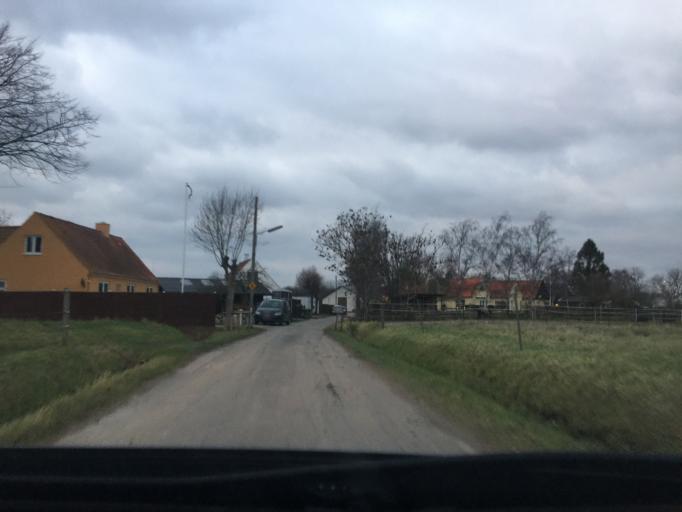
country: DK
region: Capital Region
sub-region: Dragor Kommune
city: Dragor
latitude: 55.5945
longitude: 12.6287
